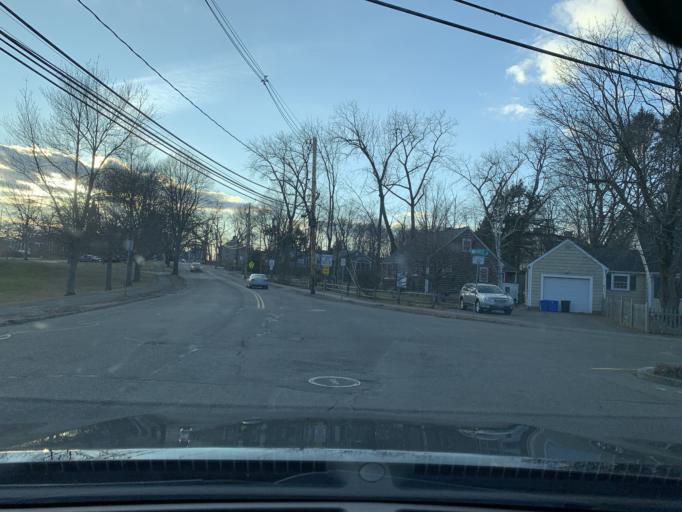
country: US
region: Massachusetts
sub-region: Essex County
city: Danvers
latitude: 42.5656
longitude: -70.9584
